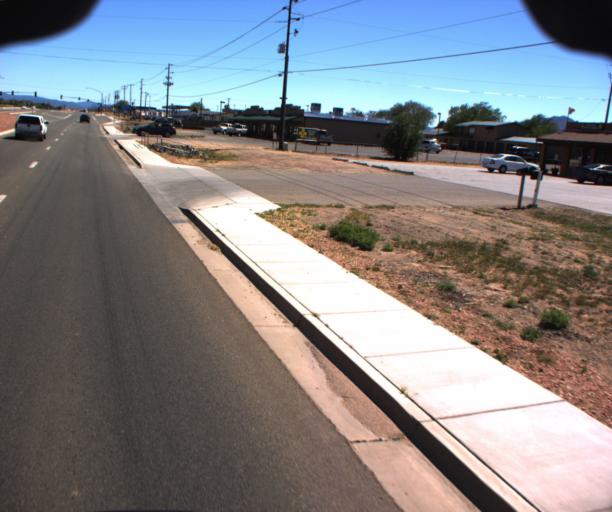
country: US
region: Arizona
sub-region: Yavapai County
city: Chino Valley
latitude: 34.7333
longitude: -112.4543
